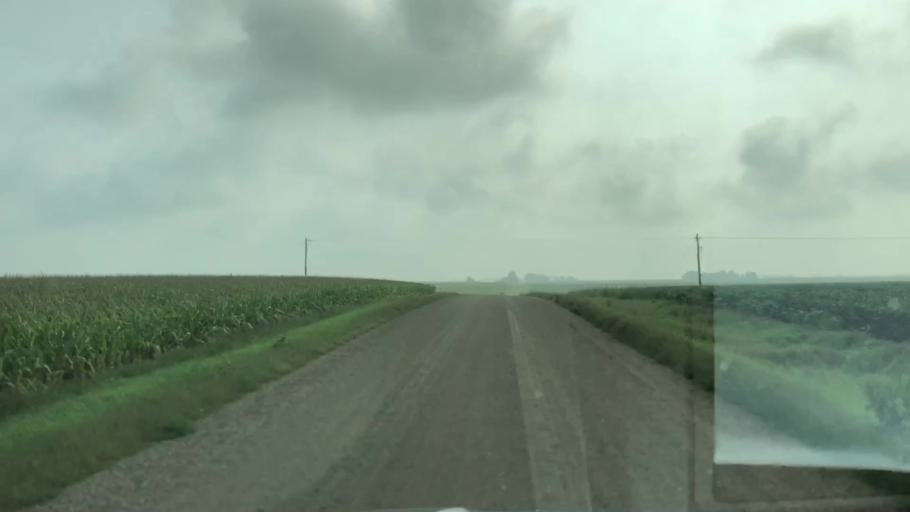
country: US
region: Iowa
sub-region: Sioux County
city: Hull
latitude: 43.2297
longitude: -96.0823
